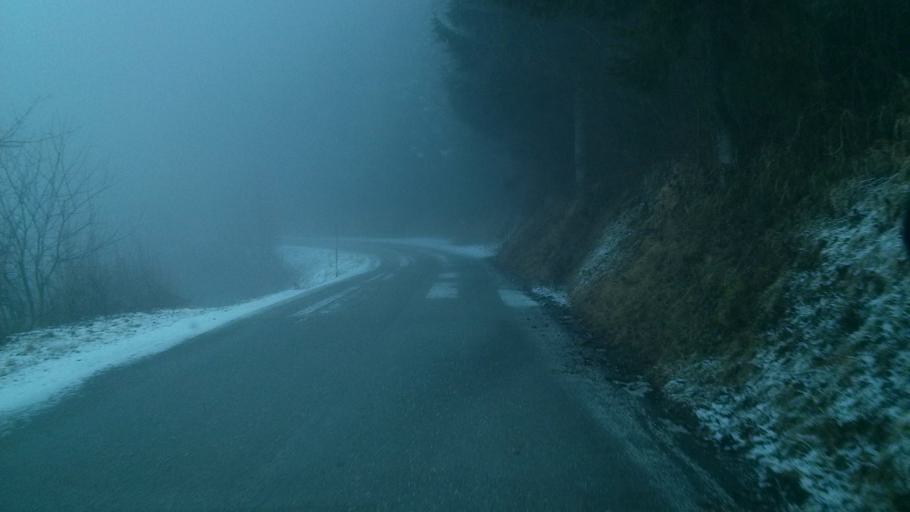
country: SI
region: Zagorje ob Savi
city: Kisovec
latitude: 46.0642
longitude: 14.9633
